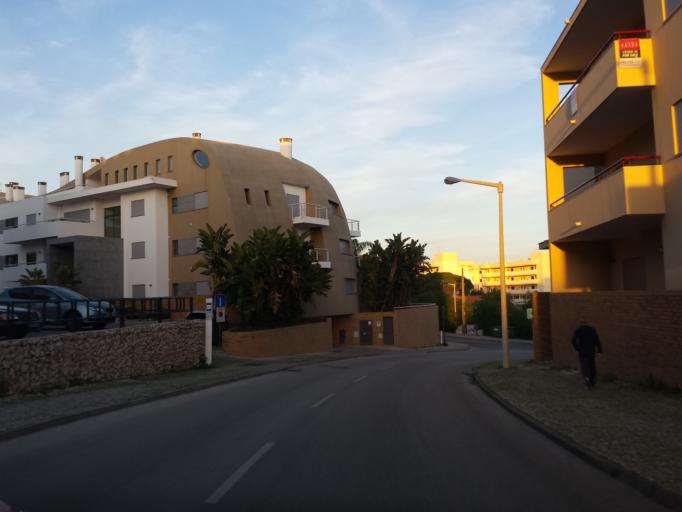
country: PT
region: Faro
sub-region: Lagos
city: Lagos
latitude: 37.0922
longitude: -8.6732
